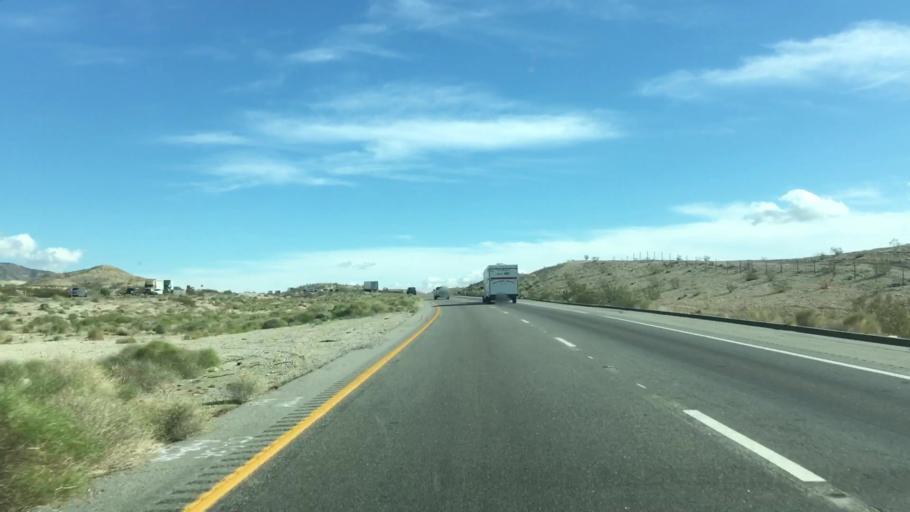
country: US
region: California
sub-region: Riverside County
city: Mecca
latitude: 33.6794
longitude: -115.9971
